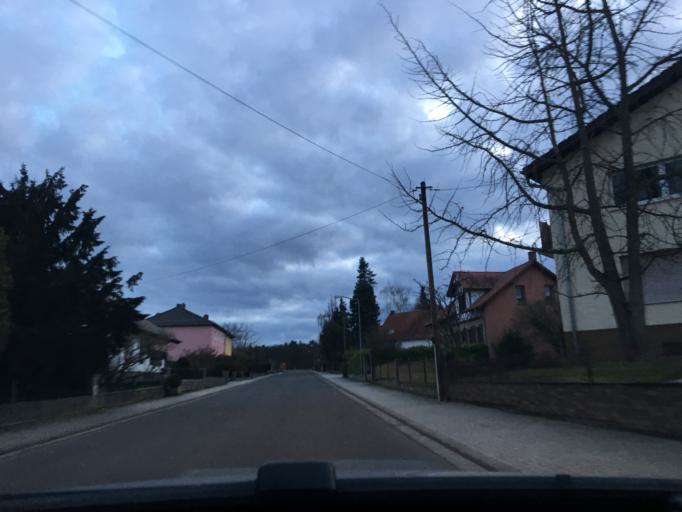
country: DE
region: Rheinland-Pfalz
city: Bechenheim
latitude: 49.7270
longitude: 8.0024
